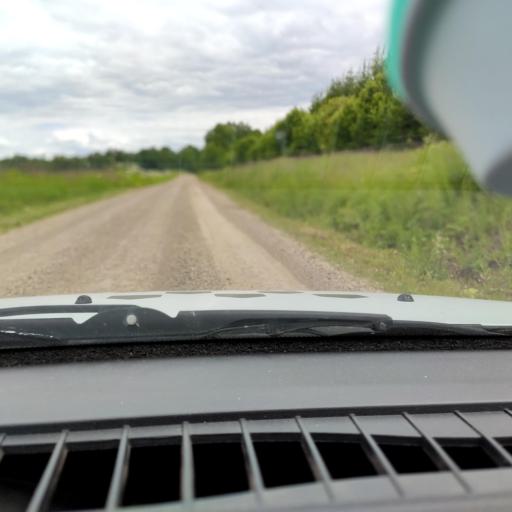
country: RU
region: Perm
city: Suksun
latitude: 57.2092
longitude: 57.6455
